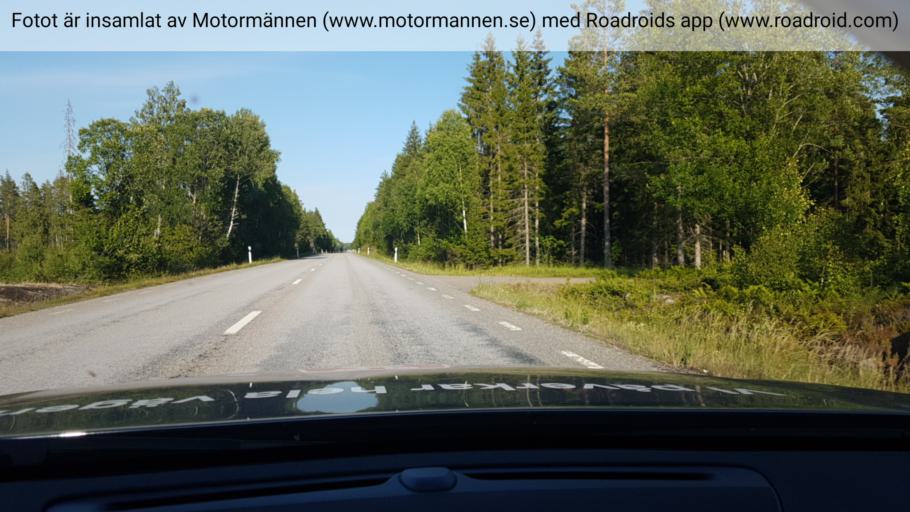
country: SE
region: Uppsala
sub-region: Osthammars Kommun
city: Gimo
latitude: 60.1650
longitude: 18.1444
